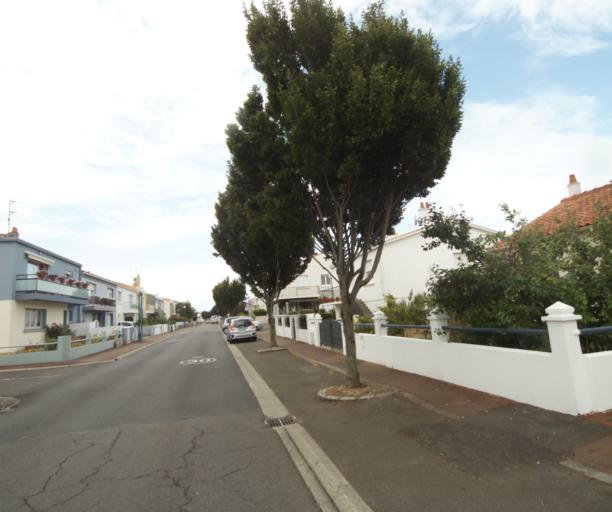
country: FR
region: Pays de la Loire
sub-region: Departement de la Vendee
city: Chateau-d'Olonne
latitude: 46.4958
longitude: -1.7583
